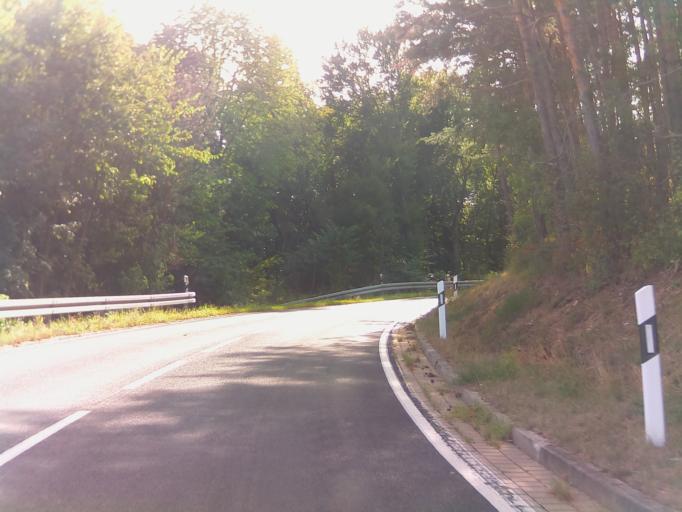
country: DE
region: Thuringia
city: Stepfershausen
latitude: 50.5846
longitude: 10.2932
